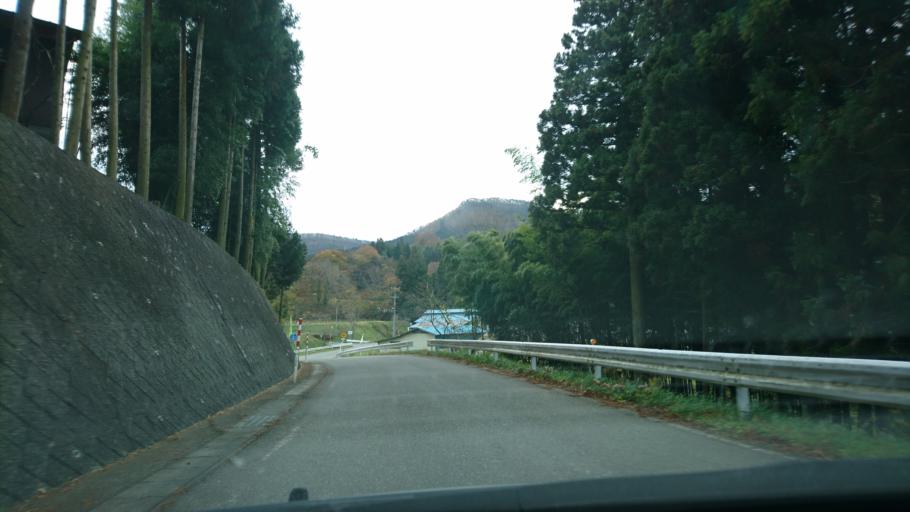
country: JP
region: Iwate
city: Ichinoseki
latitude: 39.0080
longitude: 141.2150
